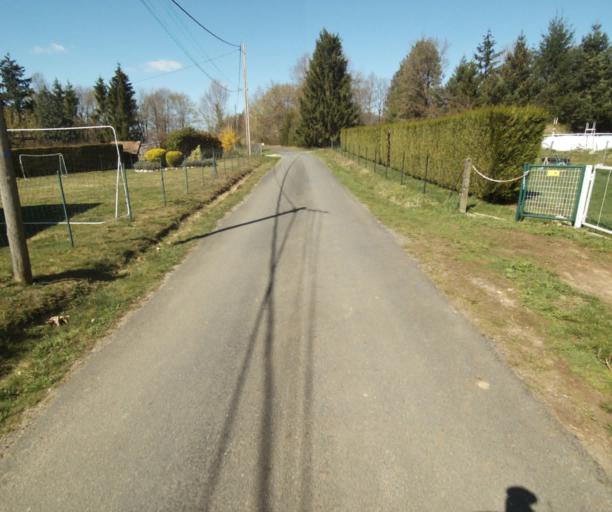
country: FR
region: Limousin
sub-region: Departement de la Correze
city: Saint-Clement
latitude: 45.3111
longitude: 1.6786
